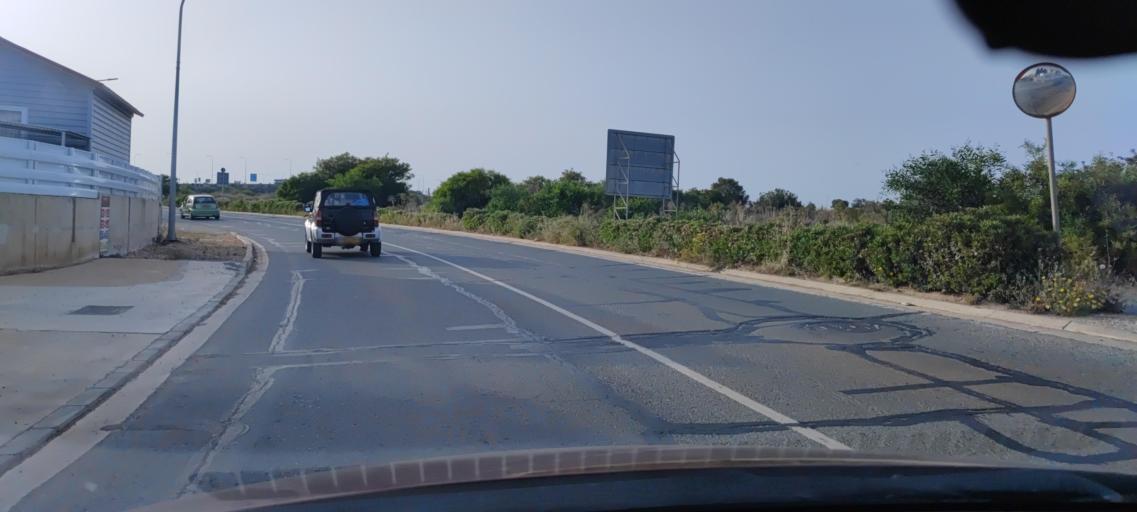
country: CY
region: Ammochostos
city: Liopetri
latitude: 34.9821
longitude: 33.9313
